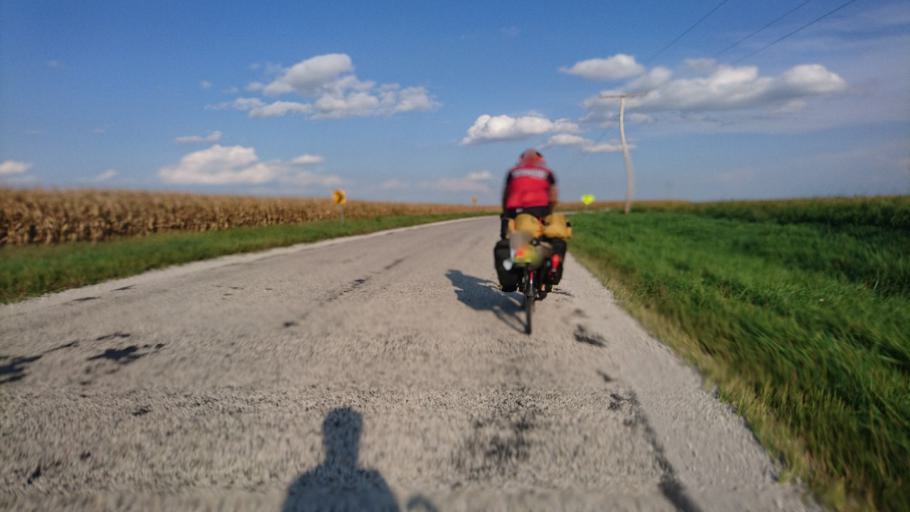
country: US
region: Illinois
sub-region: Logan County
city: Atlanta
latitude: 40.2598
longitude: -89.2074
